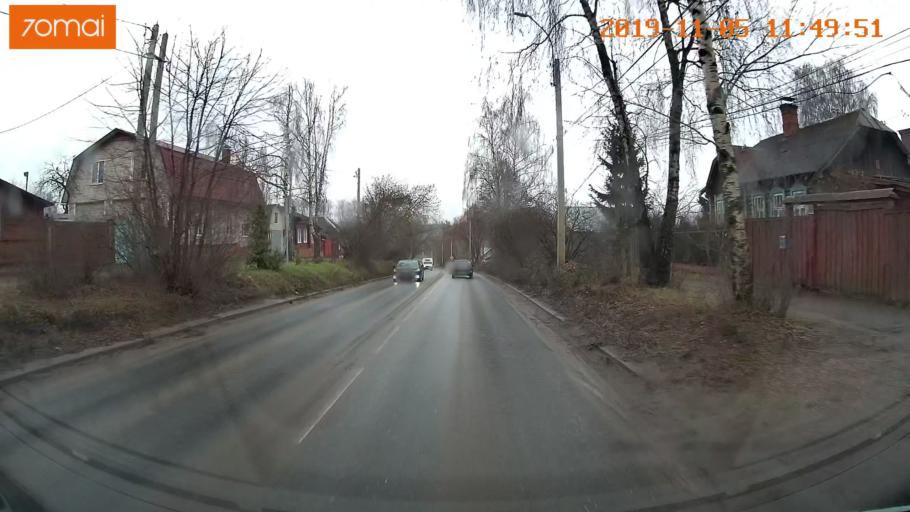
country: RU
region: Ivanovo
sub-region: Gorod Ivanovo
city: Ivanovo
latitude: 57.0060
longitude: 41.0070
